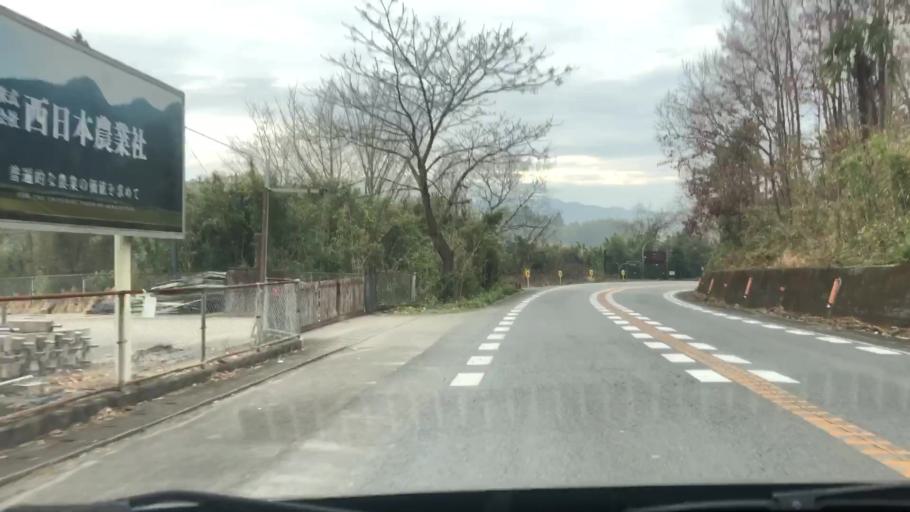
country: JP
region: Oita
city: Usuki
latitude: 33.0282
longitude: 131.6947
